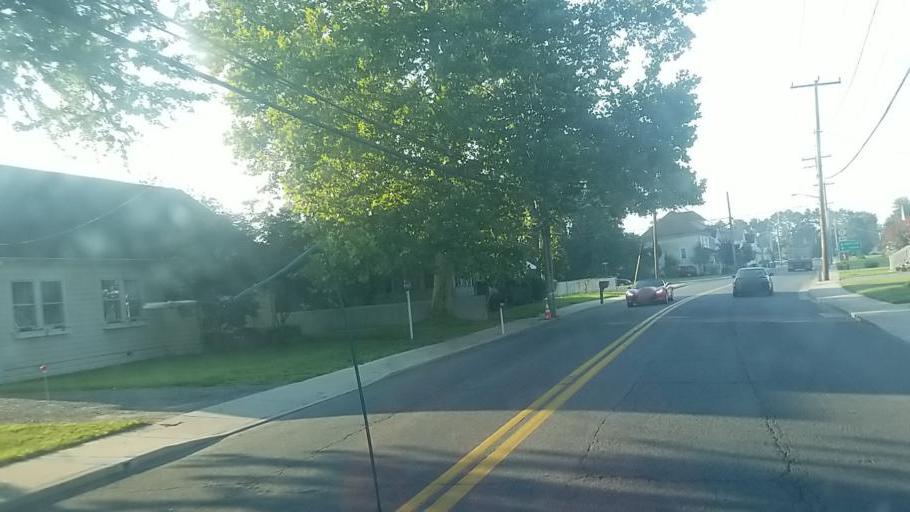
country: US
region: Delaware
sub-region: Sussex County
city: Selbyville
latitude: 38.4588
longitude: -75.2203
